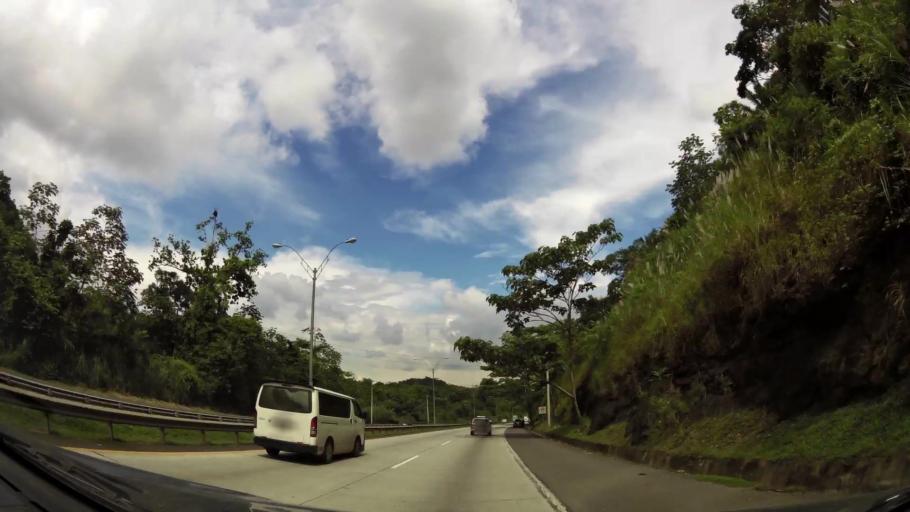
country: PA
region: Panama
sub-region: Distrito de Panama
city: Paraiso
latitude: 9.0138
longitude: -79.6445
